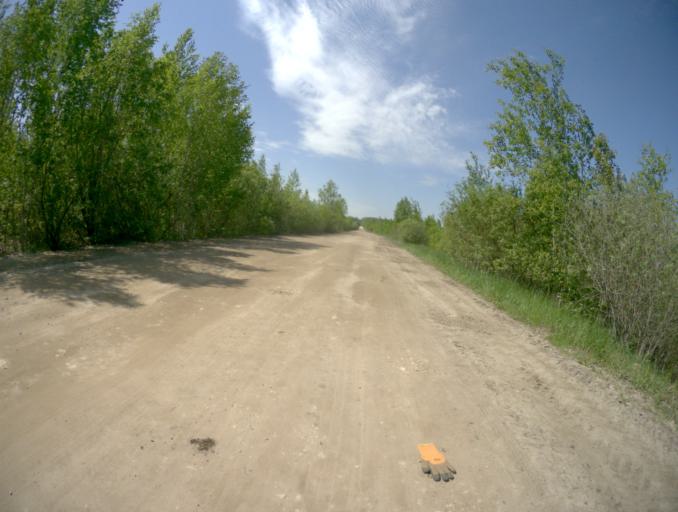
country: RU
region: Vladimir
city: Gusevskiy
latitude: 55.6888
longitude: 40.5228
